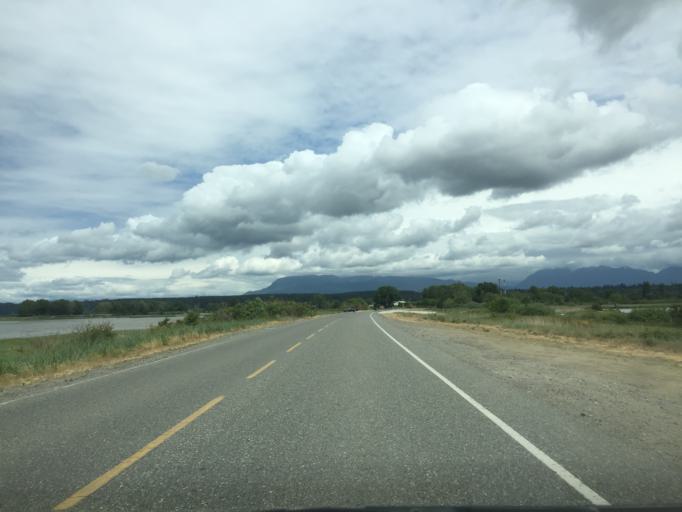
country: CA
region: British Columbia
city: Richmond
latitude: 49.2095
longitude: -123.2028
